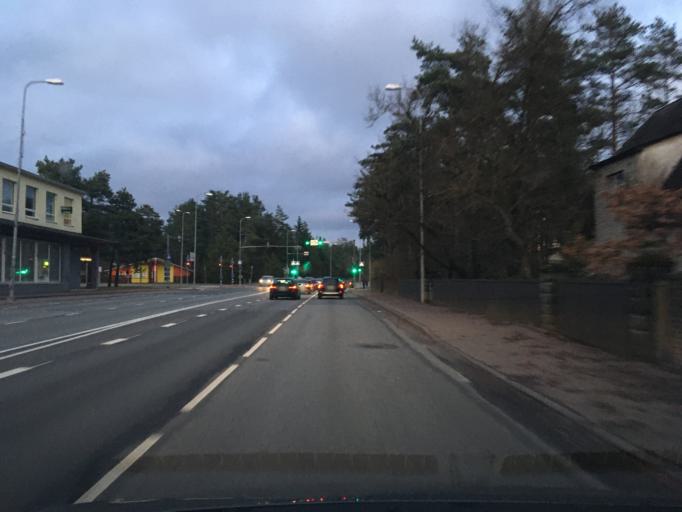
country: EE
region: Harju
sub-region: Saue vald
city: Laagri
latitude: 59.3730
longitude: 24.6650
